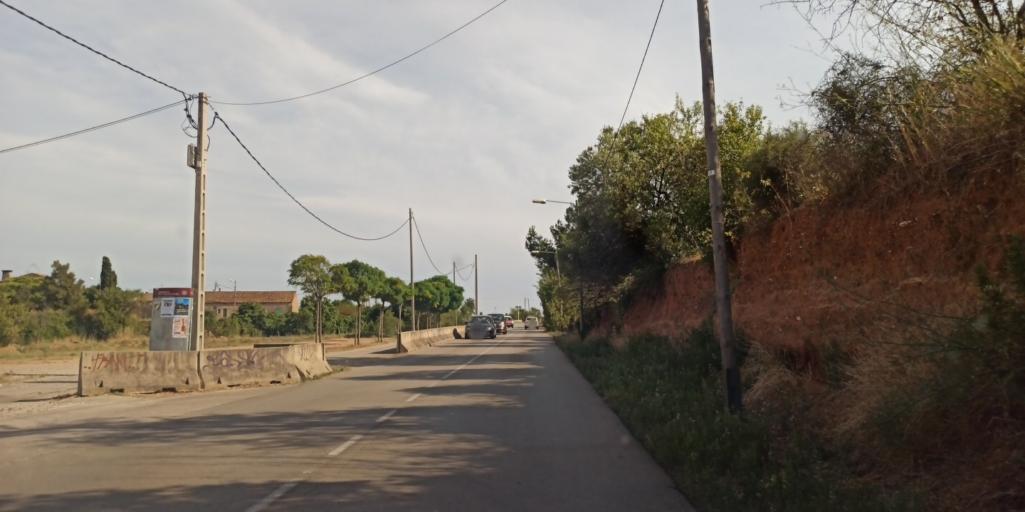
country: ES
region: Catalonia
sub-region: Provincia de Barcelona
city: Santa Coloma de Cervello
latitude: 41.3661
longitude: 2.0237
